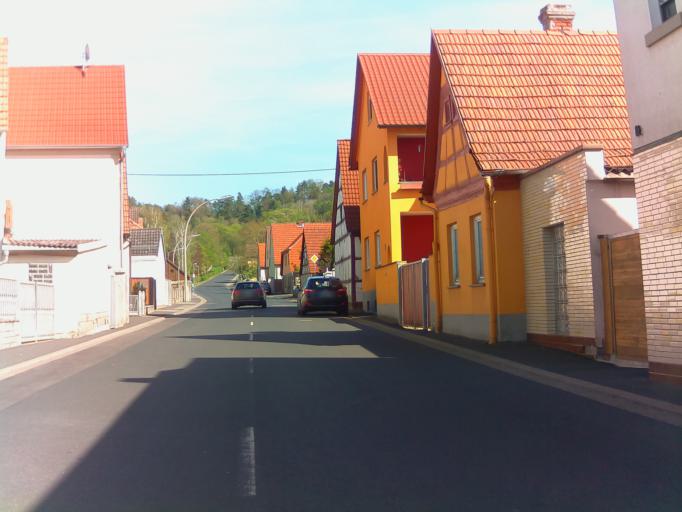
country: DE
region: Bavaria
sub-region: Regierungsbezirk Unterfranken
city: Hofheim in Unterfranken
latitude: 50.1348
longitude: 10.5654
